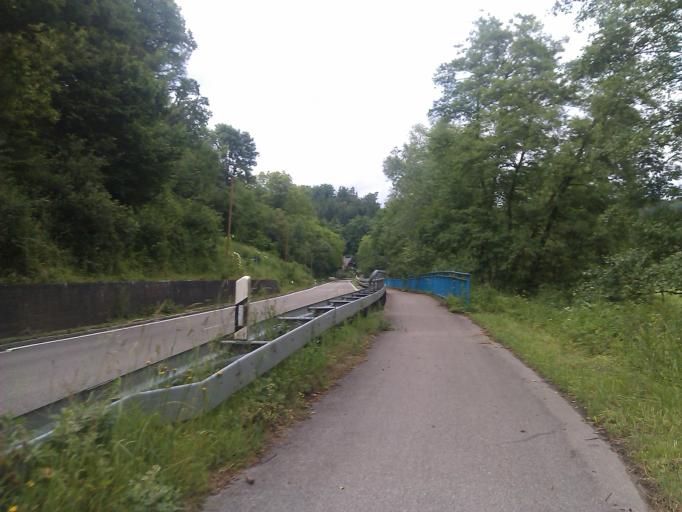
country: DE
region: Baden-Wuerttemberg
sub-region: Regierungsbezirk Stuttgart
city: Obergroningen
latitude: 48.9086
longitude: 9.9394
